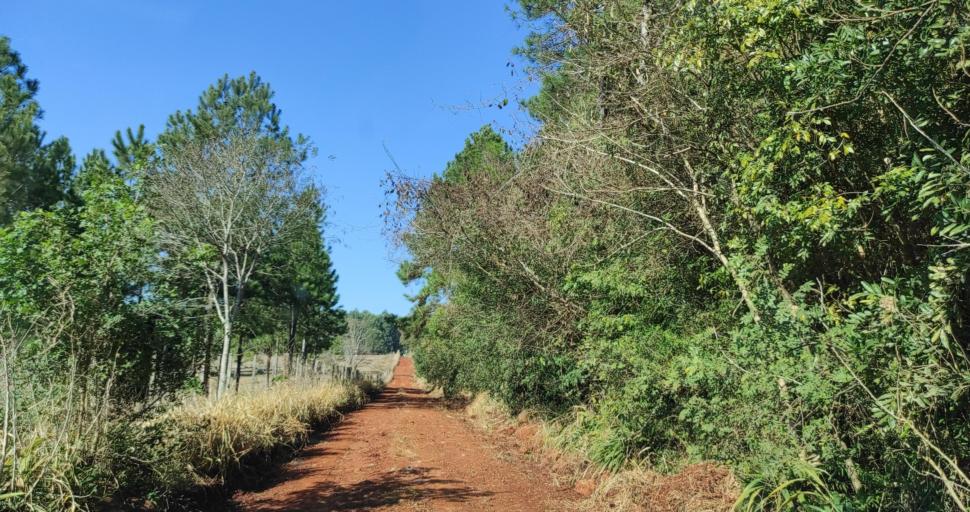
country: AR
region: Misiones
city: Capiovi
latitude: -26.8740
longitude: -55.0364
